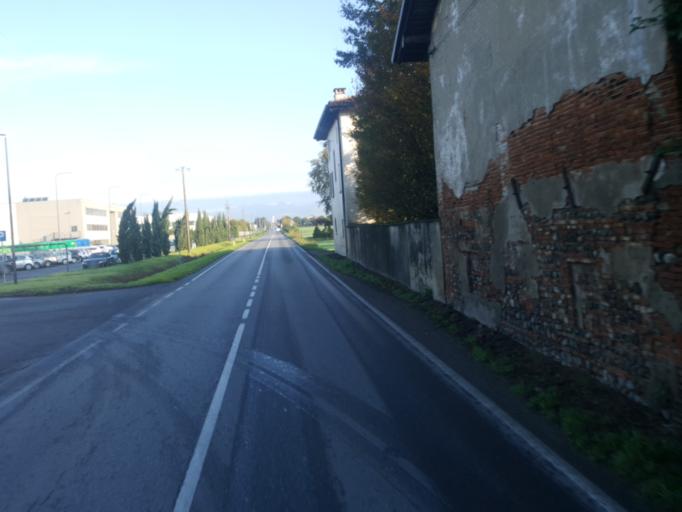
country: IT
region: Lombardy
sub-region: Provincia di Bergamo
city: Cologno al Serio
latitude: 45.5588
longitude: 9.7075
